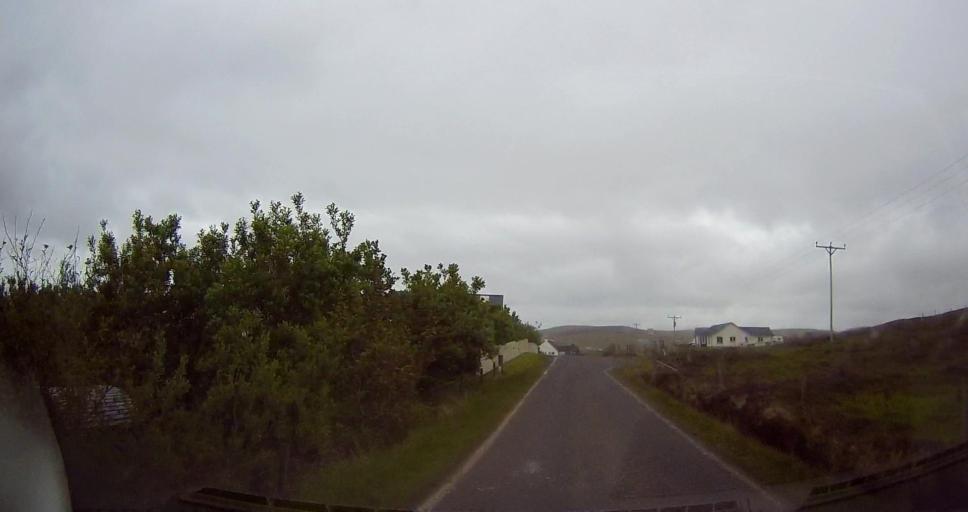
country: GB
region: Scotland
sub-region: Shetland Islands
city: Lerwick
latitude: 60.2944
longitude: -1.3641
